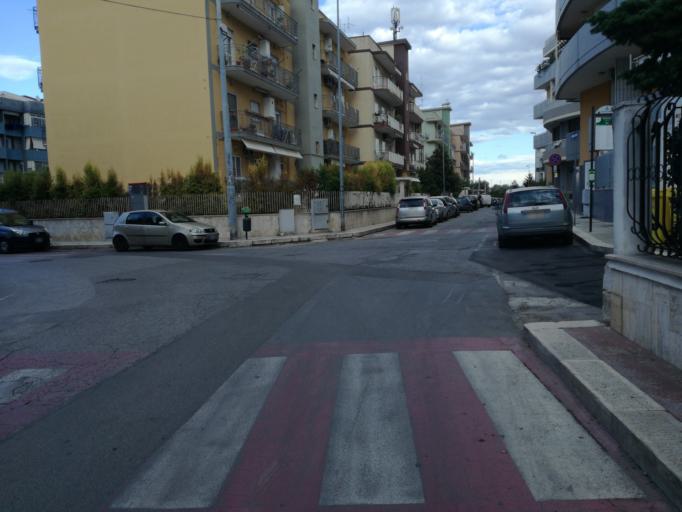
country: IT
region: Apulia
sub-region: Provincia di Bari
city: Triggiano
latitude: 41.0675
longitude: 16.9360
